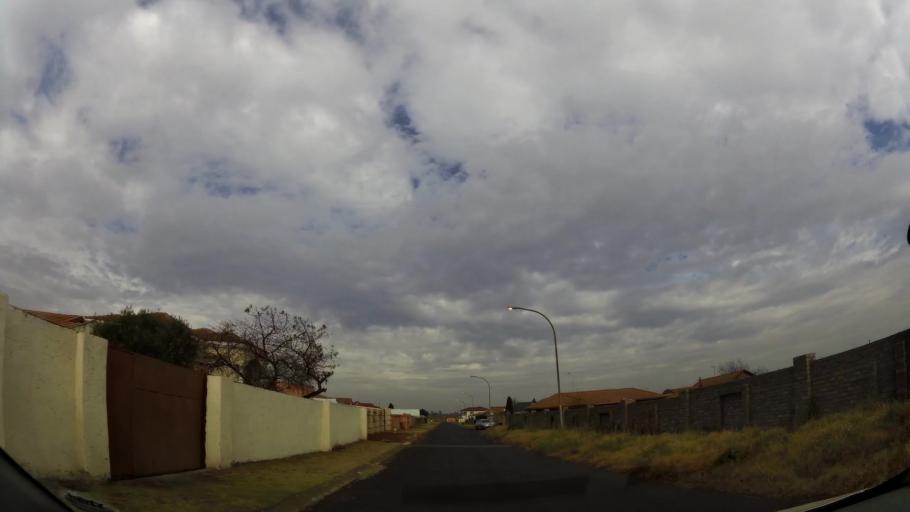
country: ZA
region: Gauteng
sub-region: Ekurhuleni Metropolitan Municipality
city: Germiston
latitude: -26.3112
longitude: 28.1747
